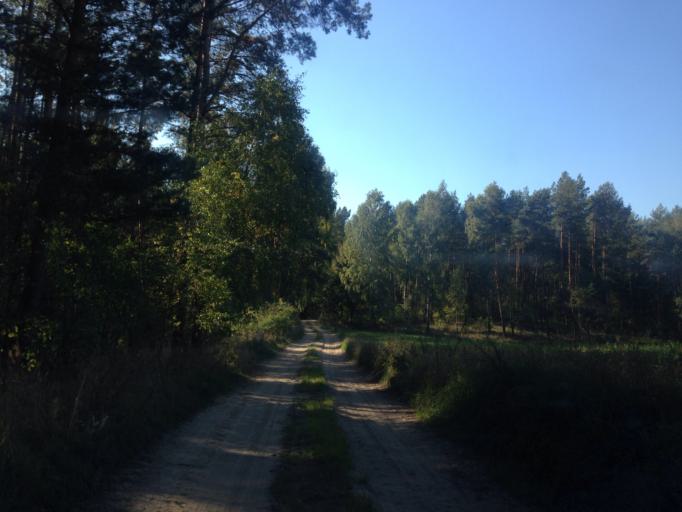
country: PL
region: Kujawsko-Pomorskie
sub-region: Powiat brodnicki
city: Bartniczka
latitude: 53.2808
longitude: 19.6667
